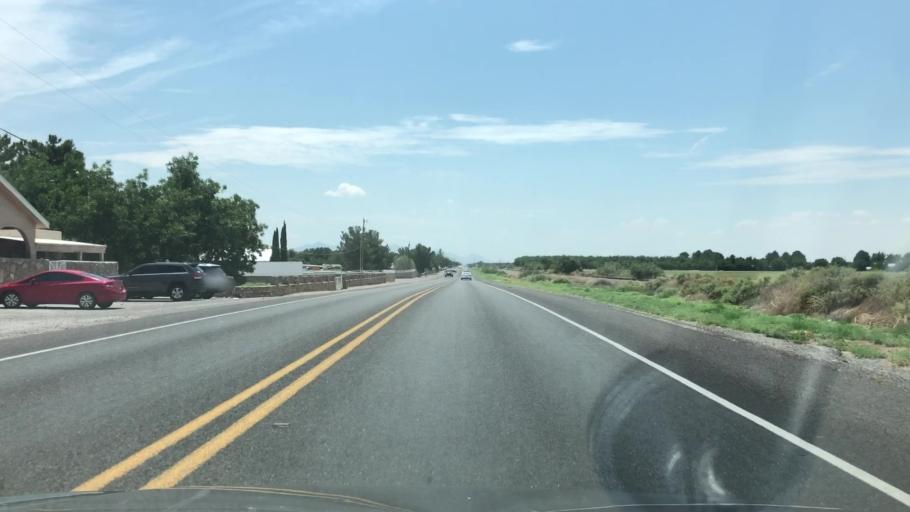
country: US
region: New Mexico
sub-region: Dona Ana County
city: Mesquite
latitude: 32.2000
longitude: -106.7190
